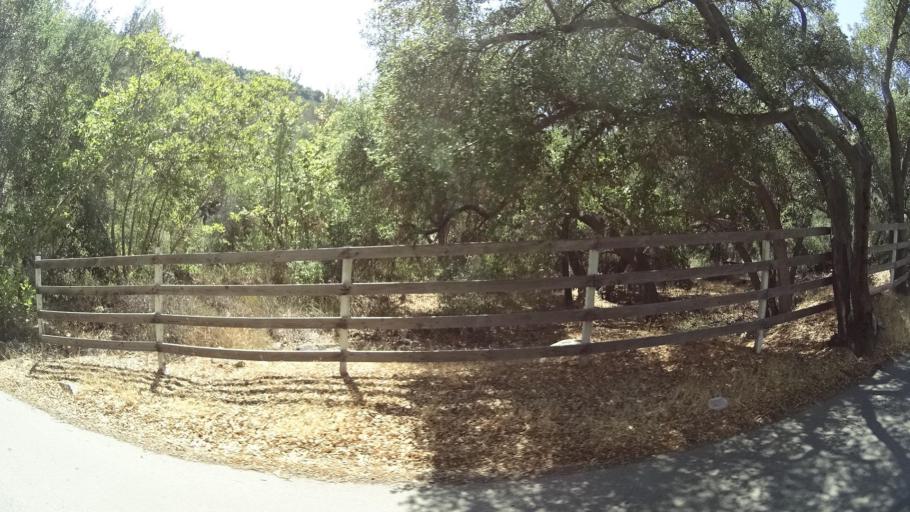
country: US
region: California
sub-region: San Diego County
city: Fallbrook
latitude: 33.4562
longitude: -117.2965
